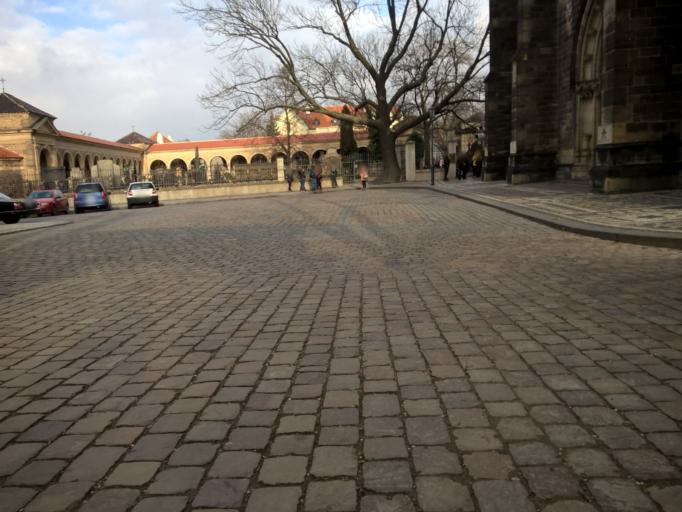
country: CZ
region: Praha
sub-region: Praha 2
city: Vysehrad
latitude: 50.0642
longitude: 14.4174
